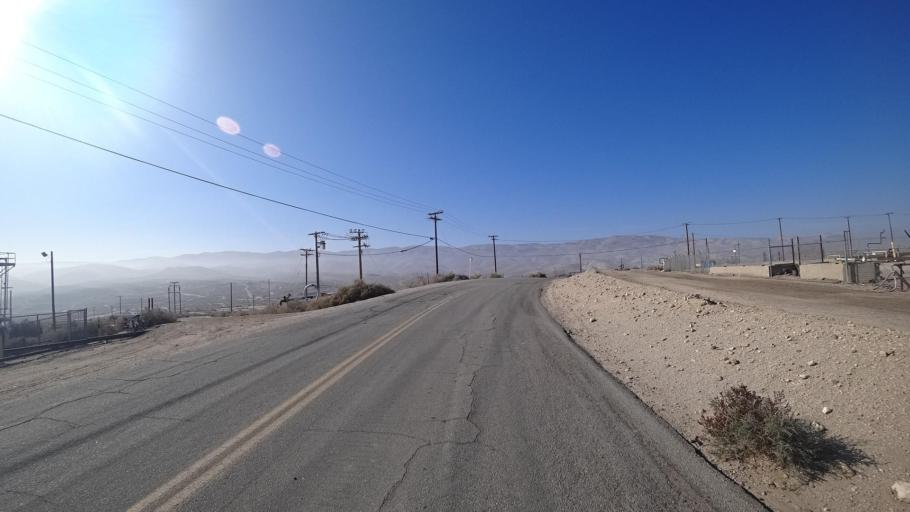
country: US
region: California
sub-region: Kern County
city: Taft Heights
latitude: 35.1138
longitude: -119.4712
